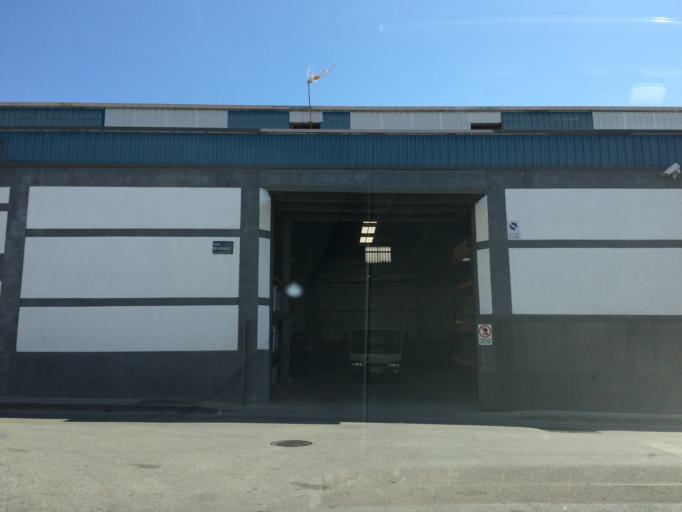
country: ES
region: Andalusia
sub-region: Provincia de Malaga
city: Malaga
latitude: 36.7026
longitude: -4.4685
